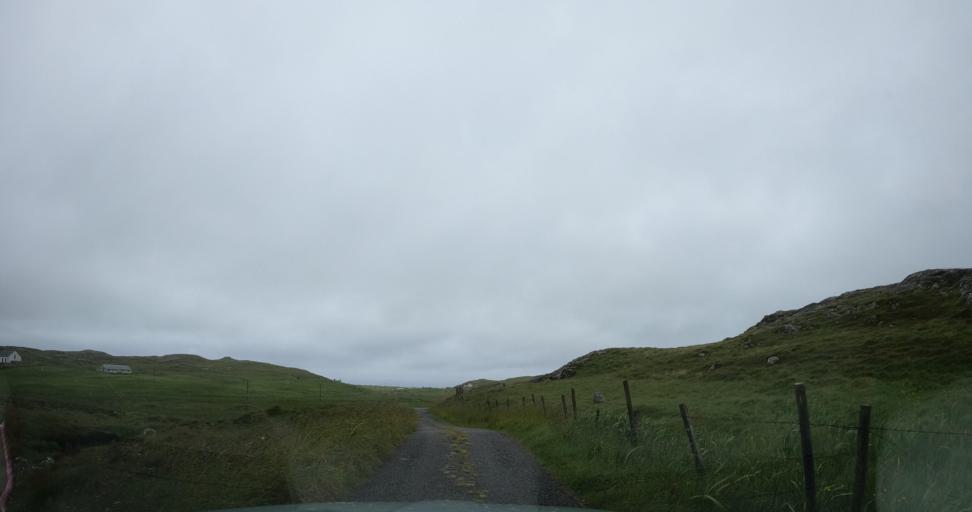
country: GB
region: Scotland
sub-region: Eilean Siar
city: Barra
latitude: 57.0032
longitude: -7.4822
